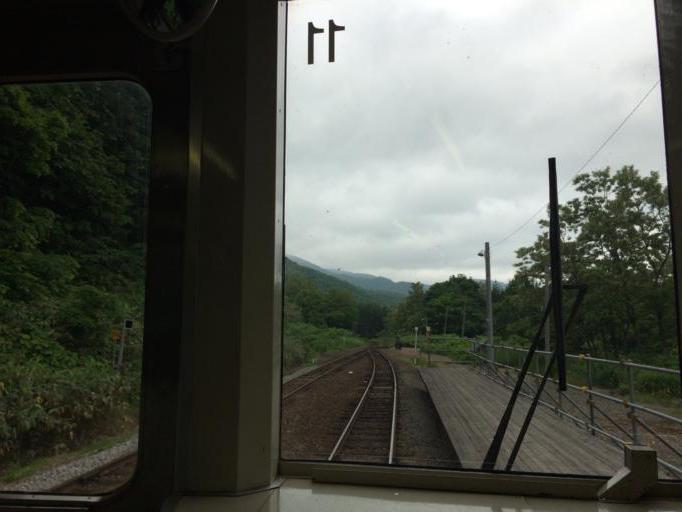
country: JP
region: Hokkaido
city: Yoichi
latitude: 43.0415
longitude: 140.7145
